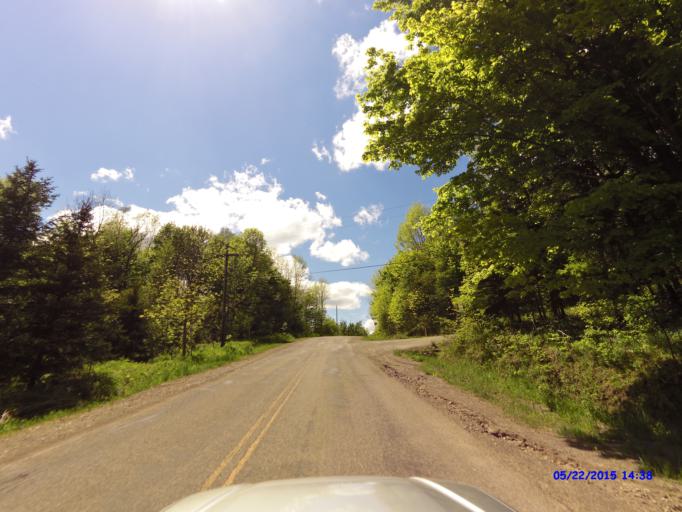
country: US
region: New York
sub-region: Cattaraugus County
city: Franklinville
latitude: 42.3400
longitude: -78.5155
